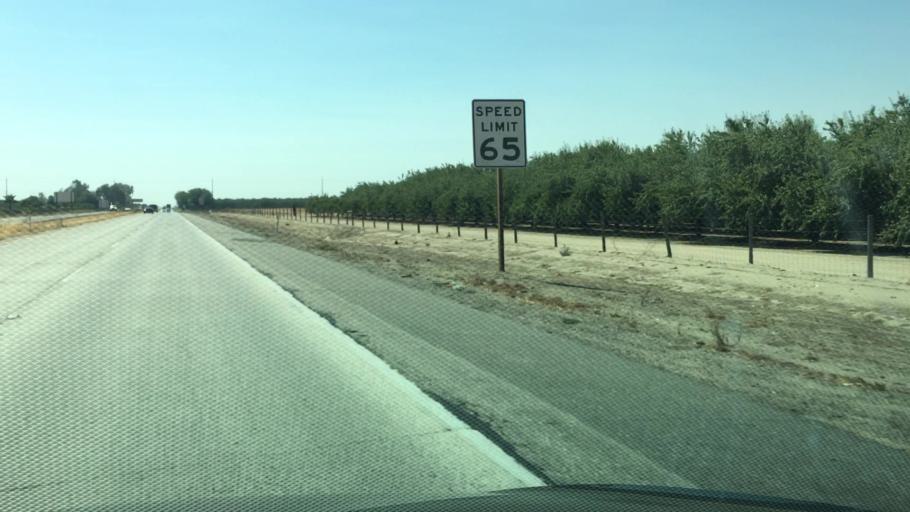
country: US
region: California
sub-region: Madera County
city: Chowchilla
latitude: 37.0836
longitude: -120.3045
